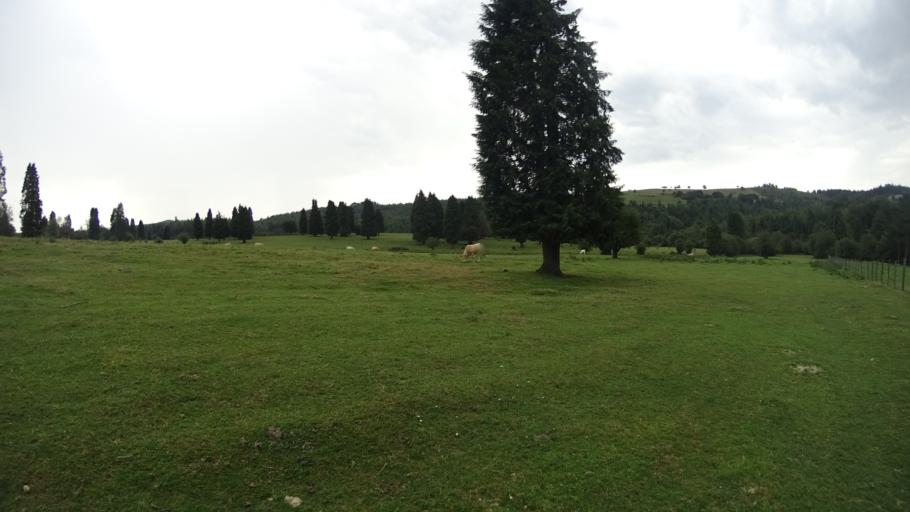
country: ES
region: Basque Country
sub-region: Bizkaia
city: Zeanuri
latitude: 43.0504
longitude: -2.7172
